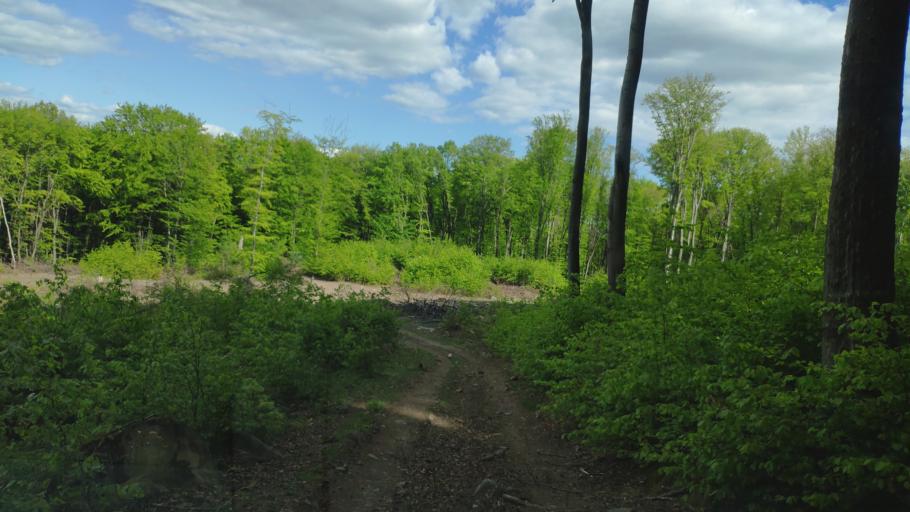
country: SK
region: Kosicky
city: Kosice
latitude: 48.6725
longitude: 21.4486
